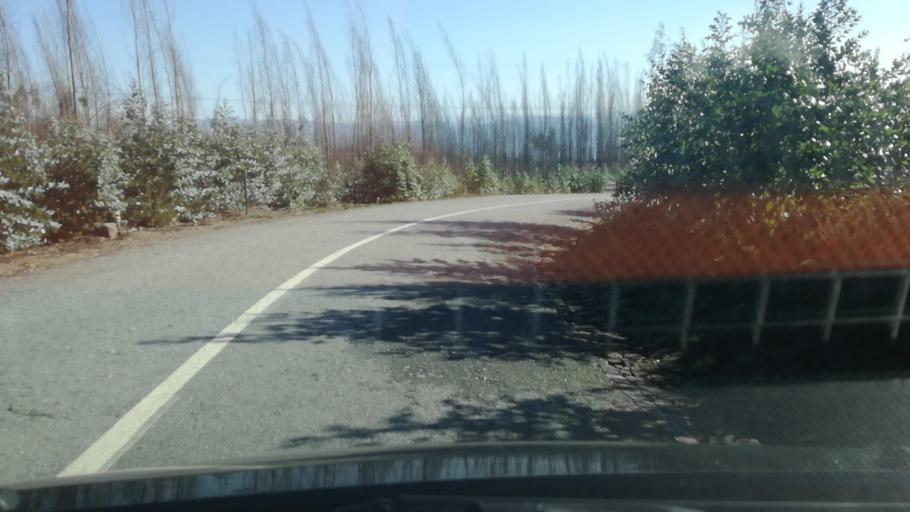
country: PT
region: Braga
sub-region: Braga
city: Braga
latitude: 41.5378
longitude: -8.3584
